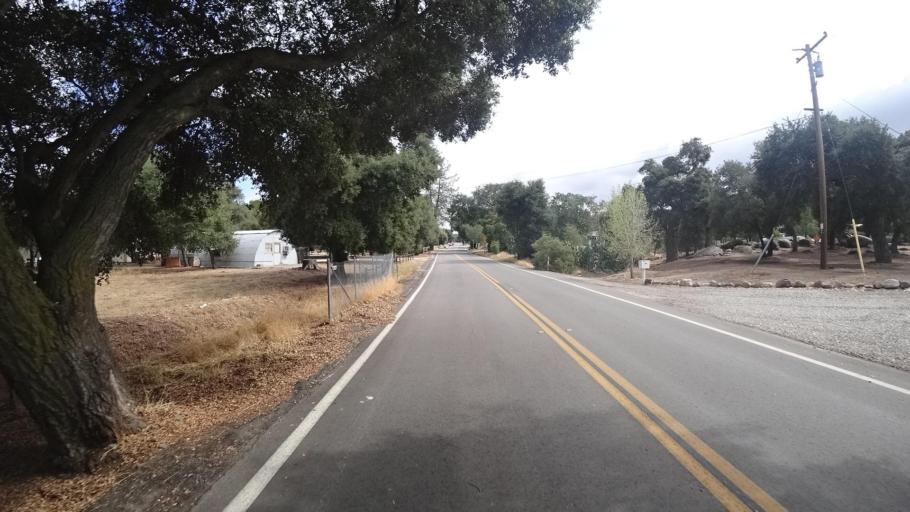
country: US
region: California
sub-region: San Diego County
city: Campo
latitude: 32.6815
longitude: -116.5143
